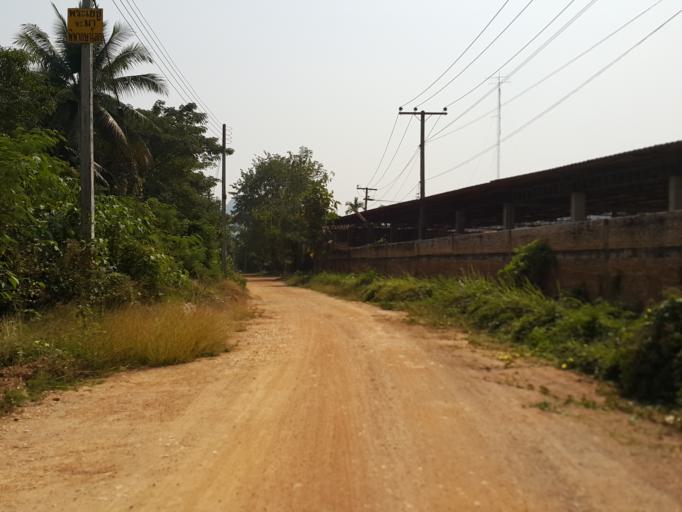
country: TH
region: Sukhothai
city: Thung Saliam
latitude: 17.3323
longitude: 99.4925
